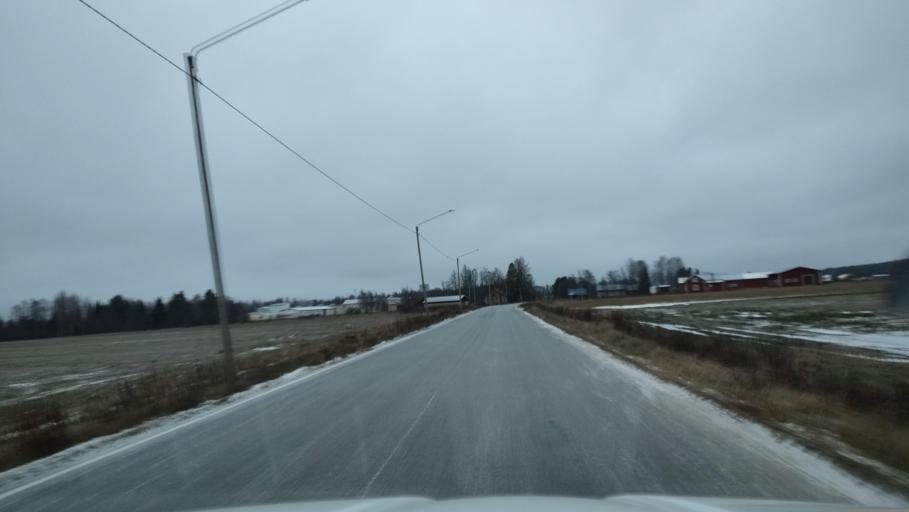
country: FI
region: Southern Ostrobothnia
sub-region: Suupohja
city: Karijoki
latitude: 62.2538
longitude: 21.6762
